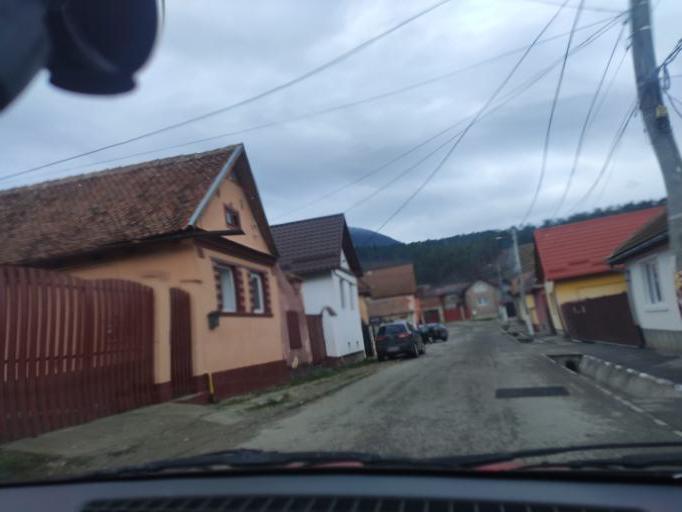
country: RO
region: Brasov
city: Codlea
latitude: 45.6958
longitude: 25.4362
